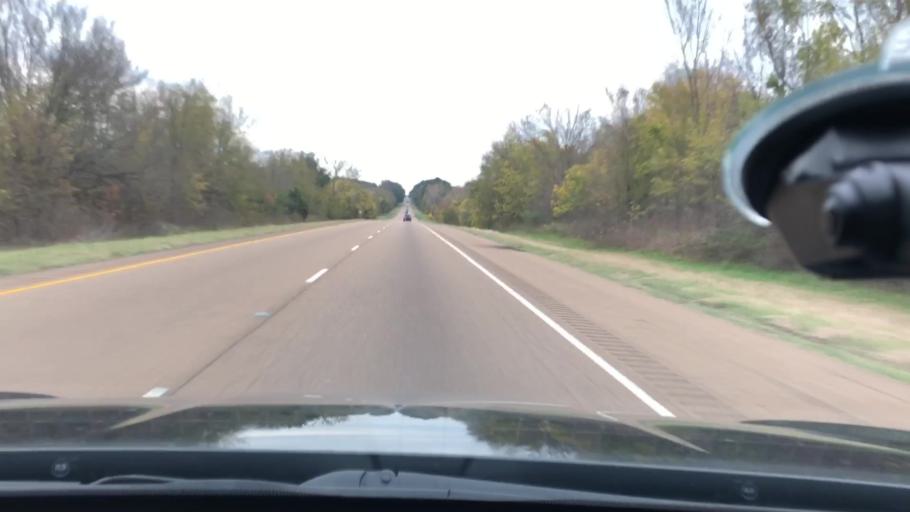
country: US
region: Arkansas
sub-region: Nevada County
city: Prescott
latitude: 33.7675
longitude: -93.4819
